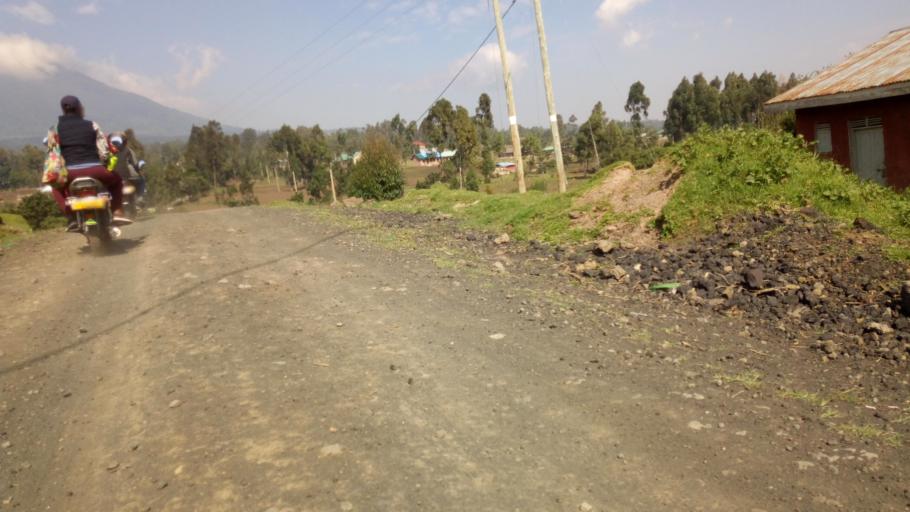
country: UG
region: Western Region
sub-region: Kisoro District
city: Kisoro
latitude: -1.3418
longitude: 29.6304
